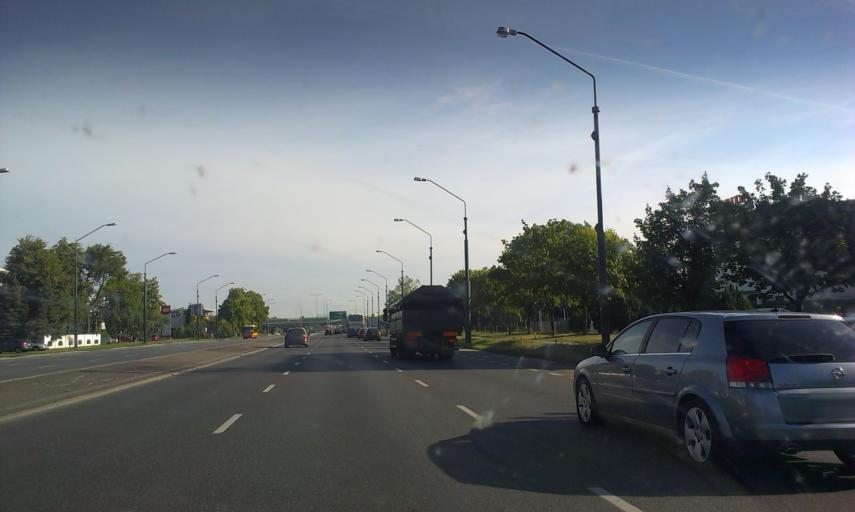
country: PL
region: Masovian Voivodeship
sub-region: Powiat piaseczynski
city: Mysiadlo
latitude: 52.1353
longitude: 21.0180
